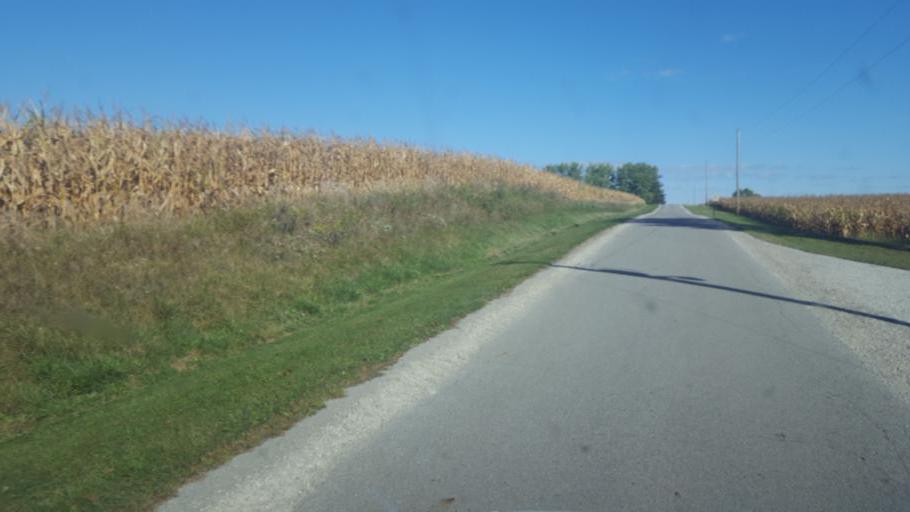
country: US
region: Ohio
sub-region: Wyandot County
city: Upper Sandusky
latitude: 40.7715
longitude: -83.2075
